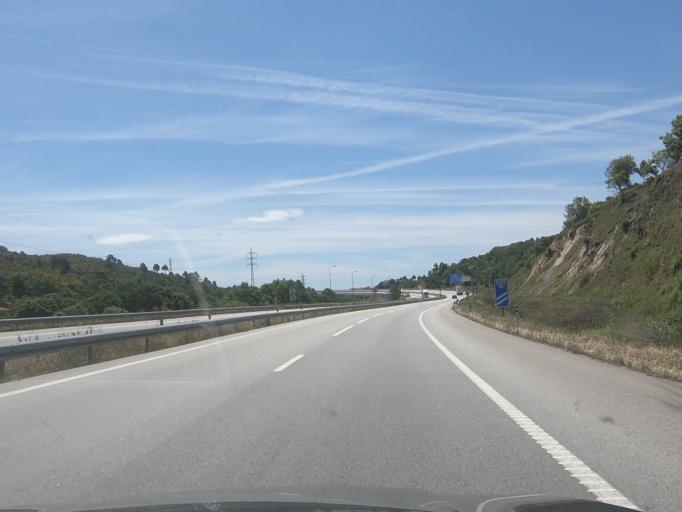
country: PT
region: Guarda
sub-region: Guarda
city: Sequeira
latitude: 40.5748
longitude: -7.2503
